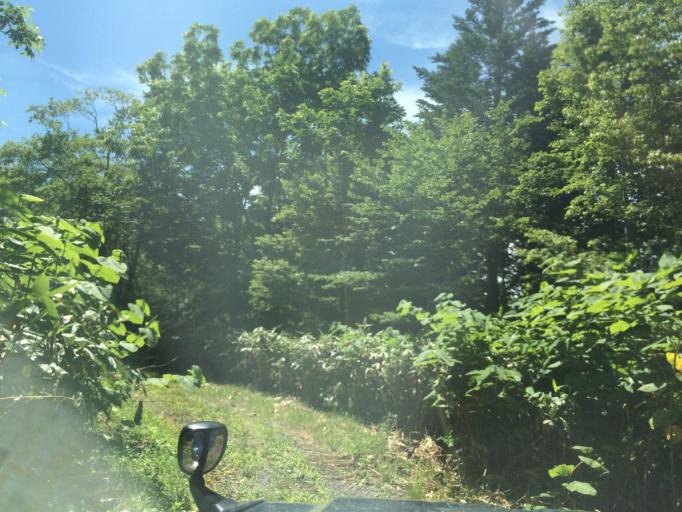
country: JP
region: Hokkaido
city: Niseko Town
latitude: 42.8574
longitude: 140.8187
